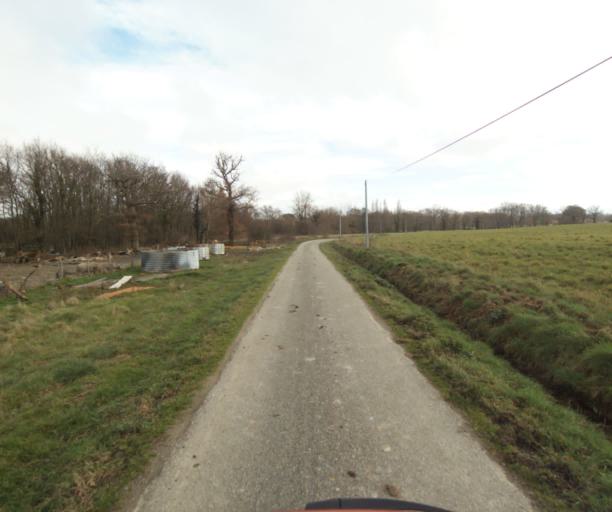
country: FR
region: Languedoc-Roussillon
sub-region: Departement de l'Aude
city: Belpech
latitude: 43.1610
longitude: 1.6978
